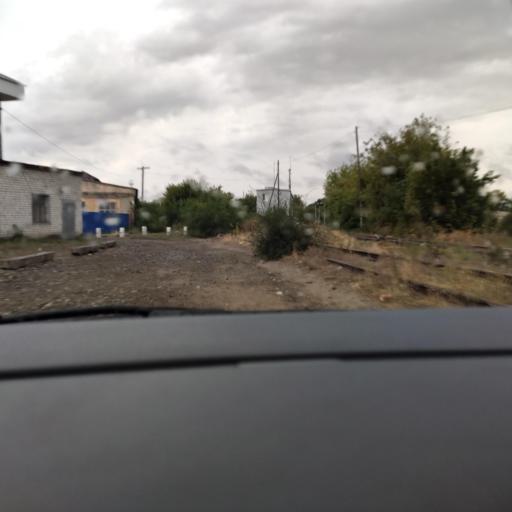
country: RU
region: Voronezj
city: Voronezh
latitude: 51.6769
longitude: 39.1812
